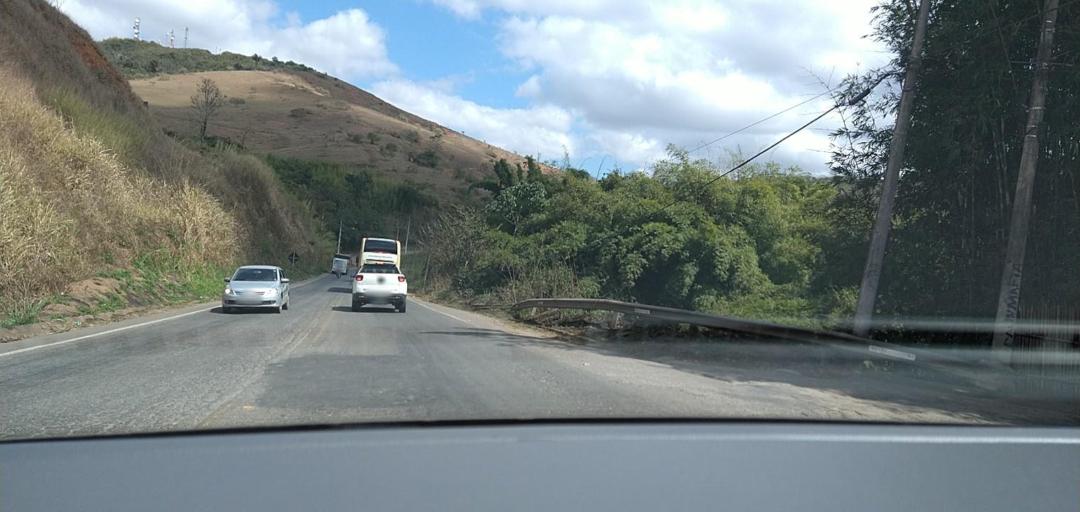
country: BR
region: Minas Gerais
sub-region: Ponte Nova
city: Ponte Nova
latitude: -20.4235
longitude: -42.8955
